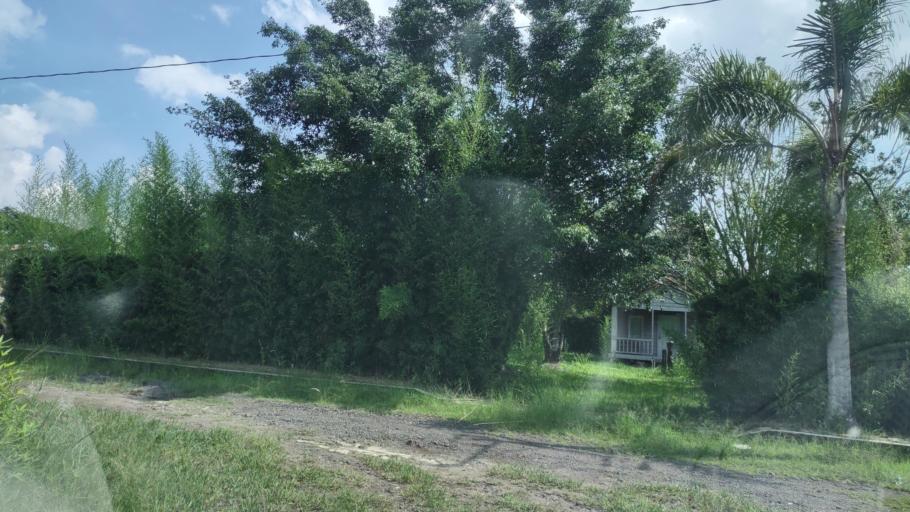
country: MX
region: Veracruz
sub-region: Emiliano Zapata
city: Dos Rios
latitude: 19.4592
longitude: -96.8066
